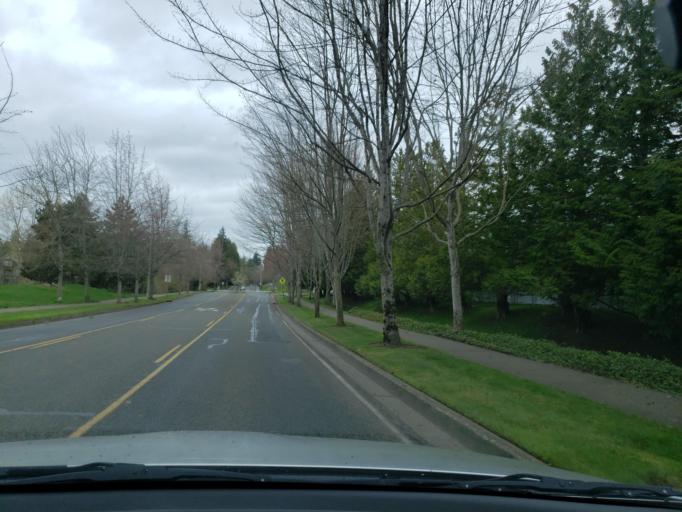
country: US
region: Washington
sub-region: Snohomish County
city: Mukilteo
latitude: 47.8933
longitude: -122.2995
